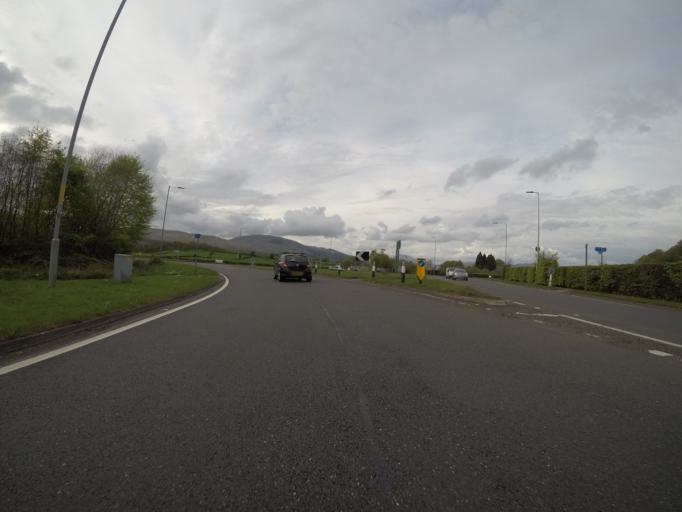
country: GB
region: Scotland
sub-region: West Dunbartonshire
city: Balloch
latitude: 56.0260
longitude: -4.6338
